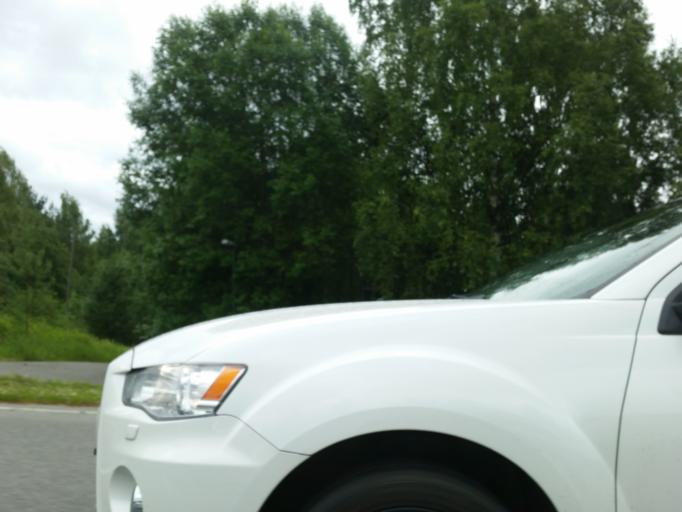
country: FI
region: Northern Savo
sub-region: Kuopio
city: Kuopio
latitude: 62.8832
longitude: 27.6425
